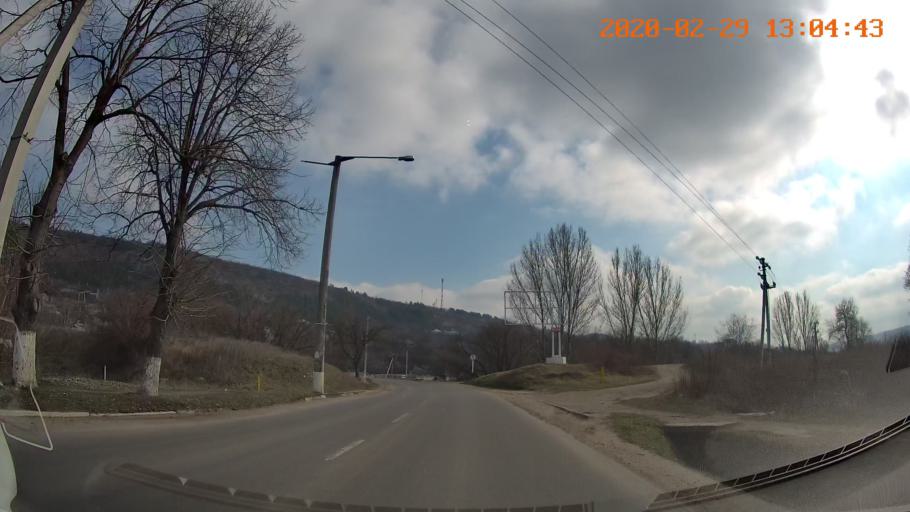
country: MD
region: Telenesti
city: Camenca
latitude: 48.0250
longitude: 28.7064
